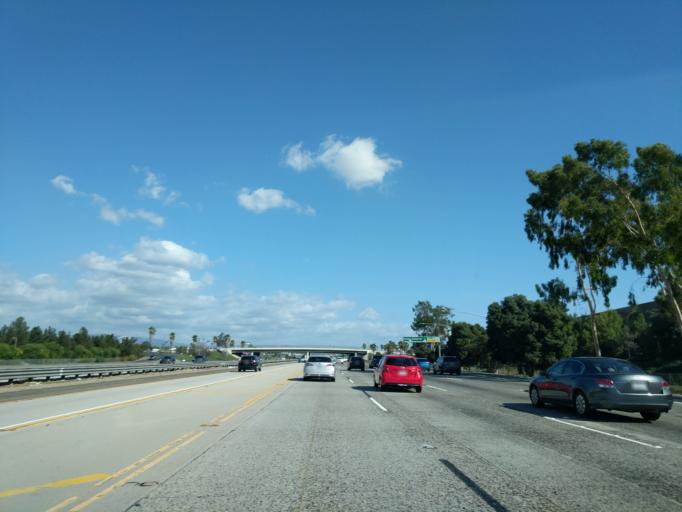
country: US
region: California
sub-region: Orange County
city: Laguna Woods
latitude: 33.6492
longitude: -117.7514
